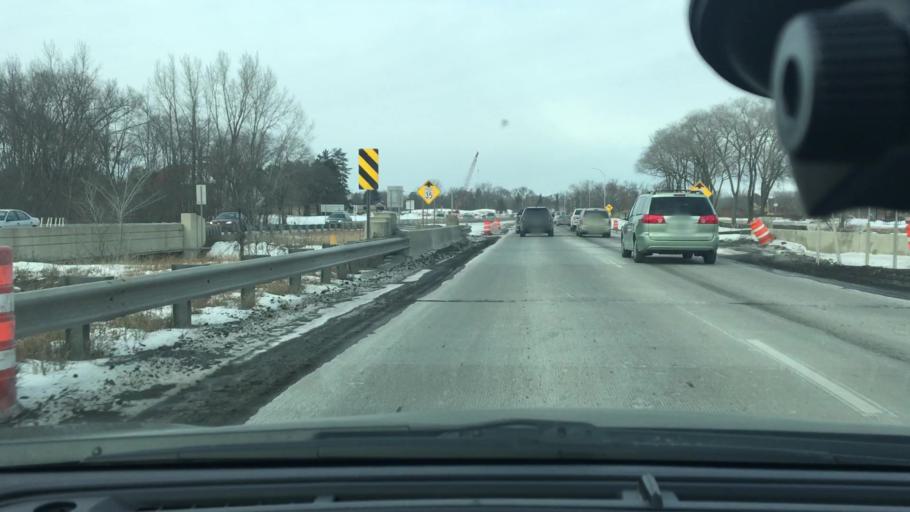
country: US
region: Minnesota
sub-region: Hennepin County
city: Champlin
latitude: 45.1818
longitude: -93.3921
